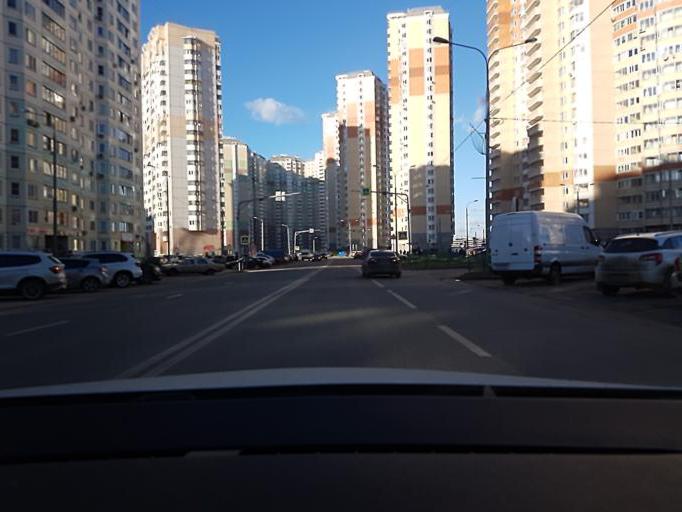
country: RU
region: Moskovskaya
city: Pavshino
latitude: 55.8207
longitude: 37.3754
